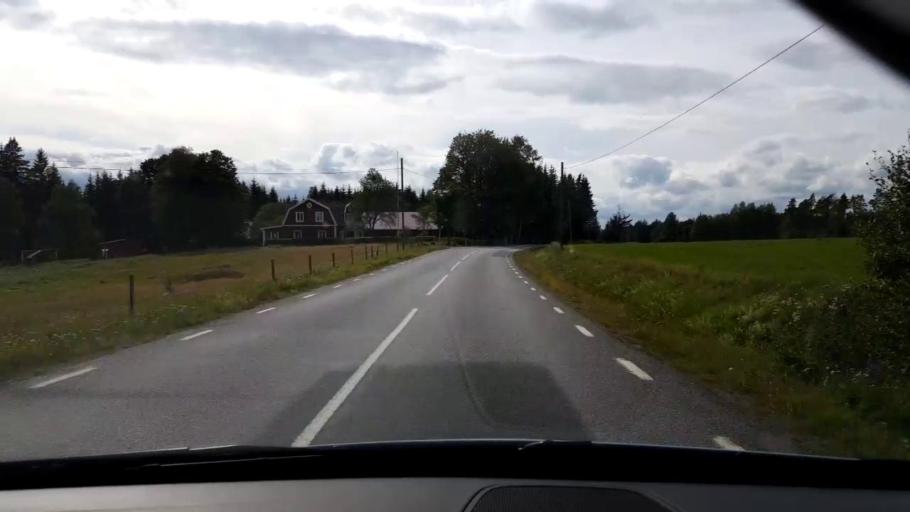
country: SE
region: Joenkoeping
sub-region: Vetlanda Kommun
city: Landsbro
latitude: 57.3795
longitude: 14.9913
